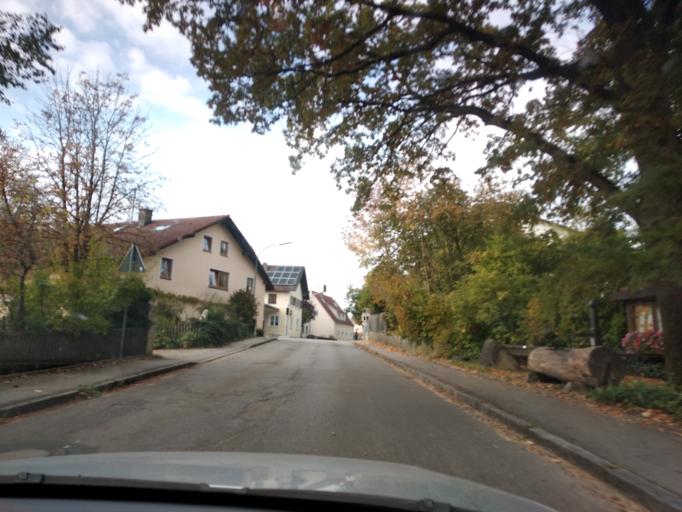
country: DE
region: Bavaria
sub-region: Upper Bavaria
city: Ottenhofen
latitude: 48.2159
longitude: 11.8805
